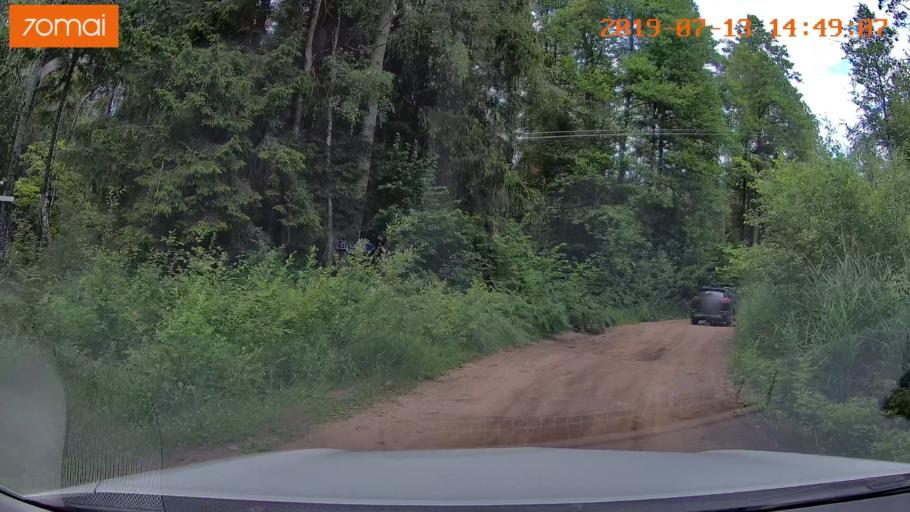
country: BY
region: Mogilev
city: Asipovichy
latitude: 53.2062
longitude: 28.7469
